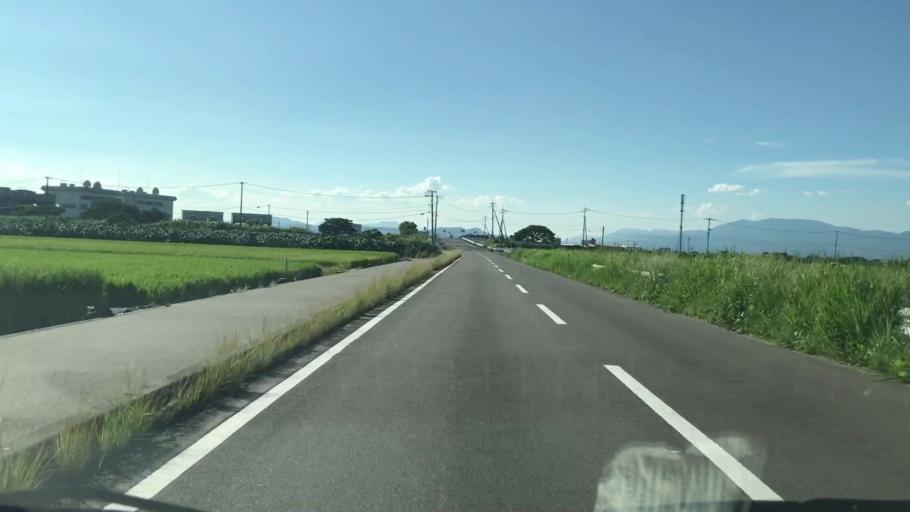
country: JP
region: Saga Prefecture
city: Okawa
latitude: 33.1849
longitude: 130.2940
